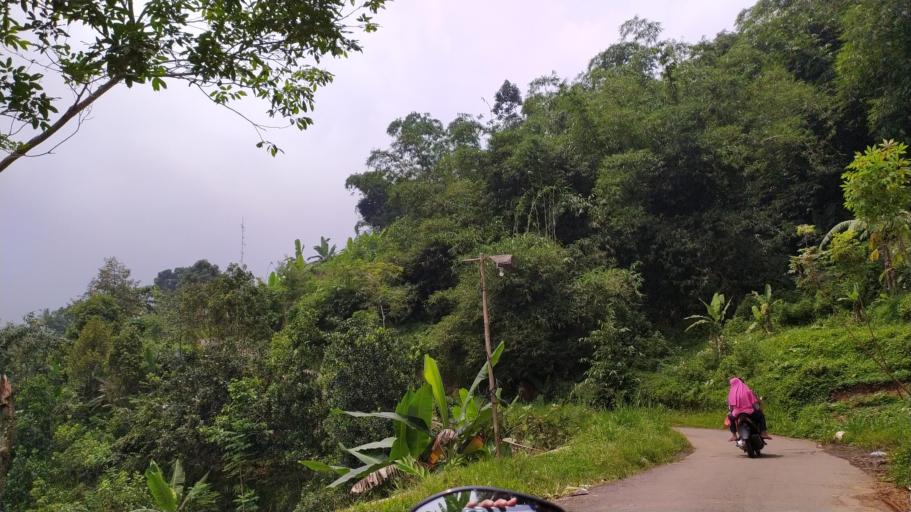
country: ID
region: West Java
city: Ciampea
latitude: -6.6273
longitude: 106.7135
